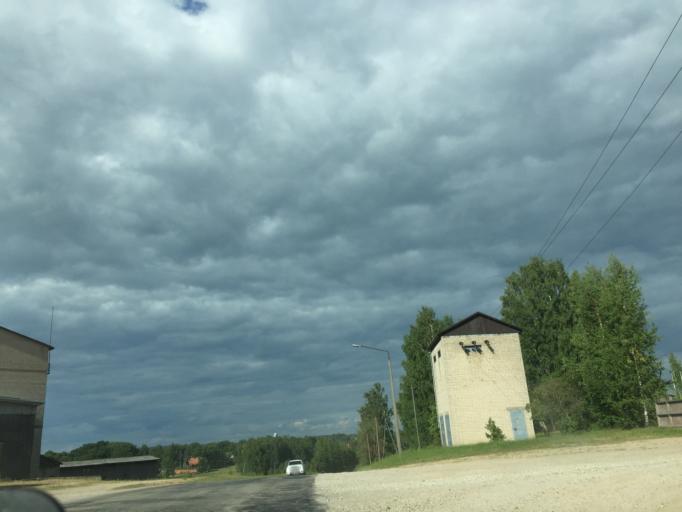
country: LV
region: Skriveri
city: Skriveri
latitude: 56.8422
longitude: 25.1457
